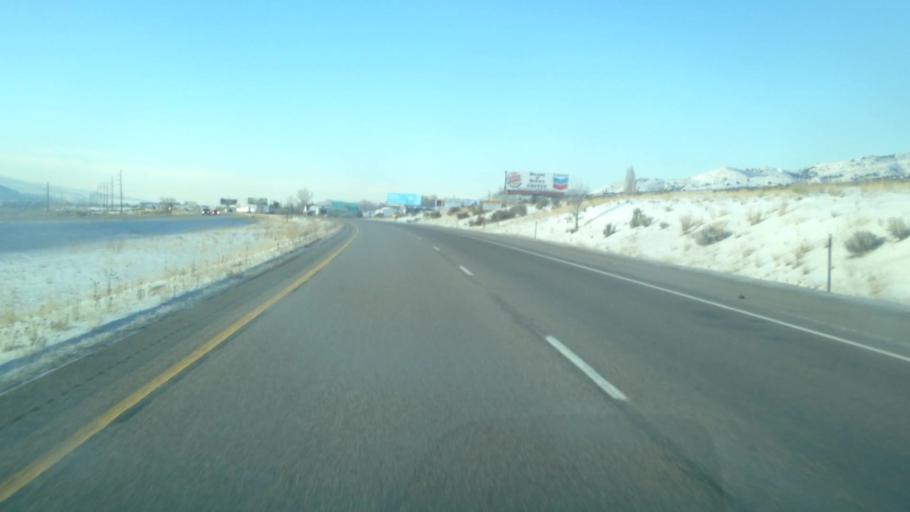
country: US
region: Idaho
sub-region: Bannock County
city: Pocatello
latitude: 42.8133
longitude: -112.3795
